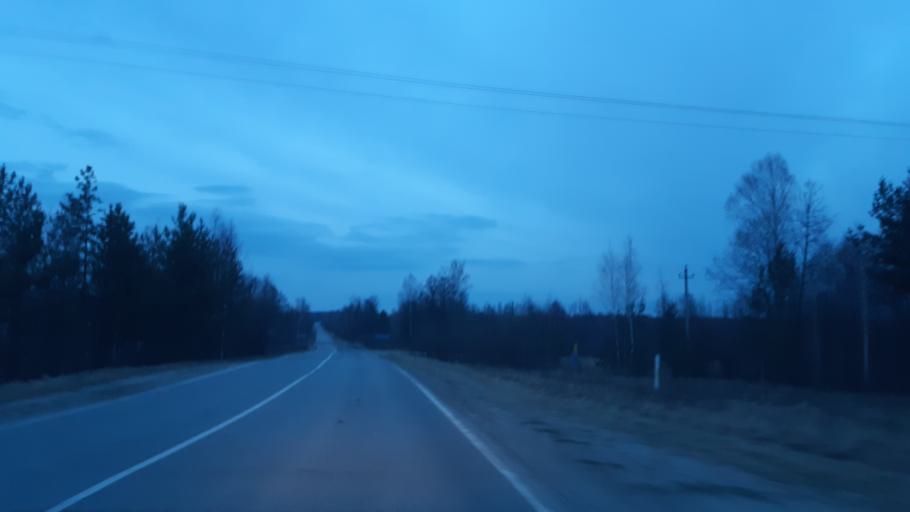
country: RU
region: Vladimir
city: Luknovo
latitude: 56.1776
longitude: 42.0076
